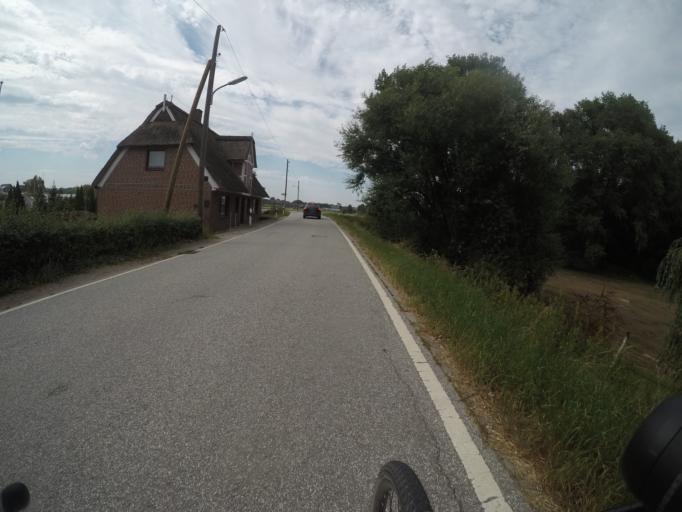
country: DE
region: Schleswig-Holstein
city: Oststeinbek
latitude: 53.4795
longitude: 10.1288
